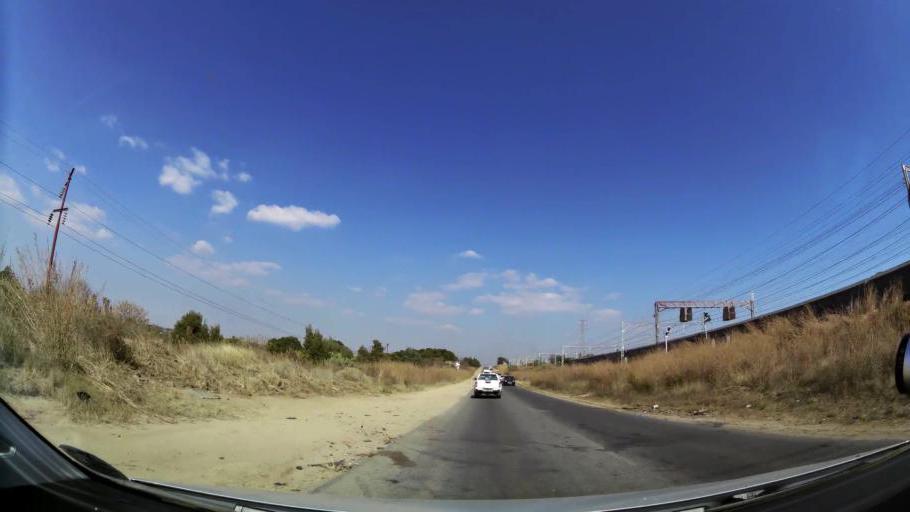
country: ZA
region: Gauteng
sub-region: Ekurhuleni Metropolitan Municipality
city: Tembisa
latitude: -26.0553
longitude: 28.2457
